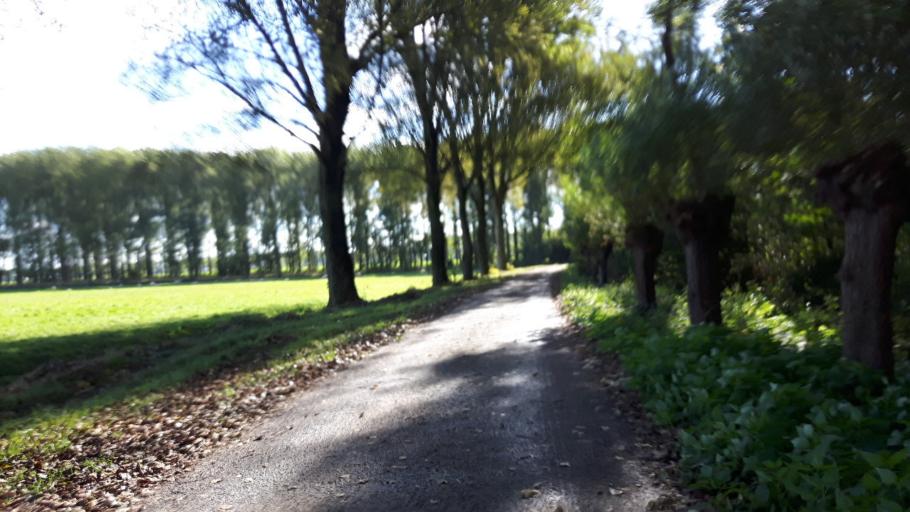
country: NL
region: Gelderland
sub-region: Gemeente Culemborg
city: Culemborg
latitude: 51.9382
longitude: 5.2548
